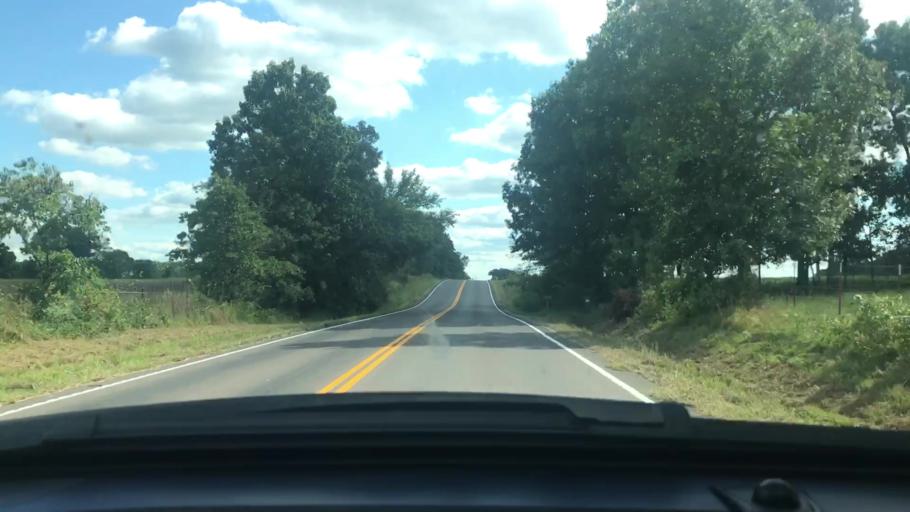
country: US
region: Missouri
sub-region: Wright County
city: Mountain Grove
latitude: 37.2705
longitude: -92.3081
